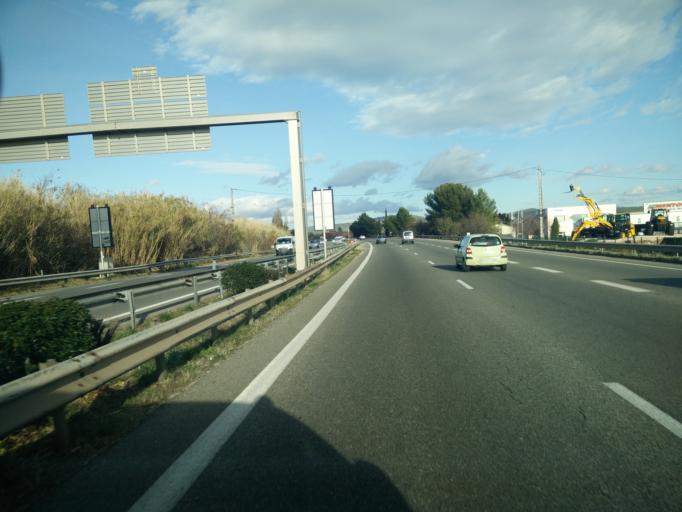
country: FR
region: Provence-Alpes-Cote d'Azur
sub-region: Departement du Var
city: La Farlede
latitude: 43.1608
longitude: 6.0488
